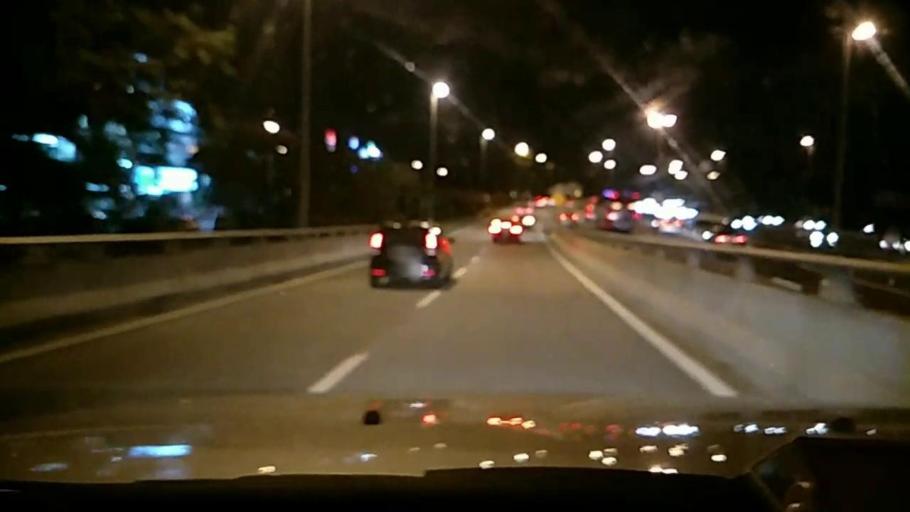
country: MY
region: Selangor
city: Subang Jaya
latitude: 2.9925
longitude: 101.6177
